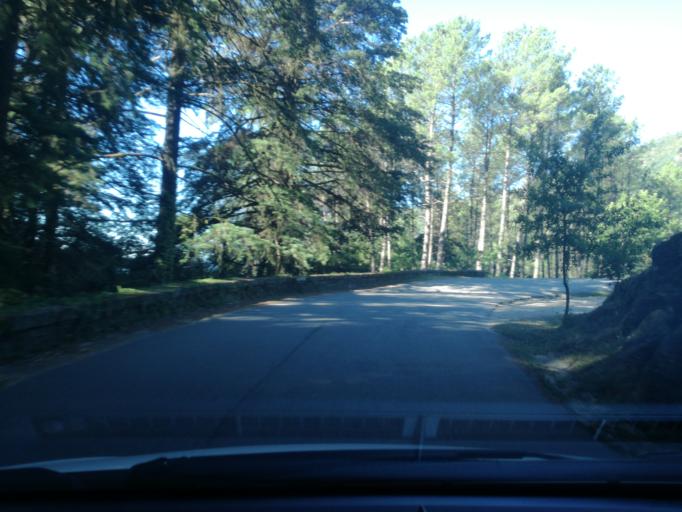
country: PT
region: Braga
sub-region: Vieira do Minho
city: Real
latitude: 41.7442
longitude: -8.1545
